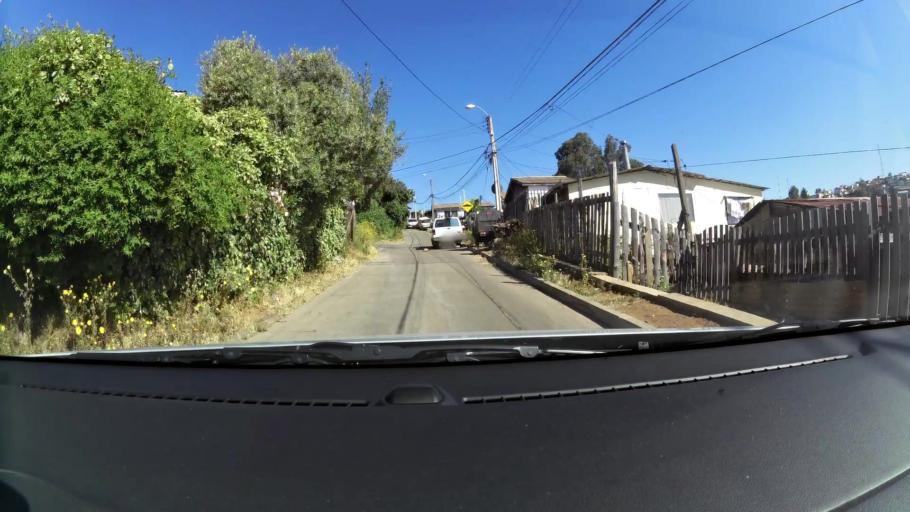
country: CL
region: Valparaiso
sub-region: Provincia de Valparaiso
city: Vina del Mar
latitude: -33.0404
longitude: -71.5639
